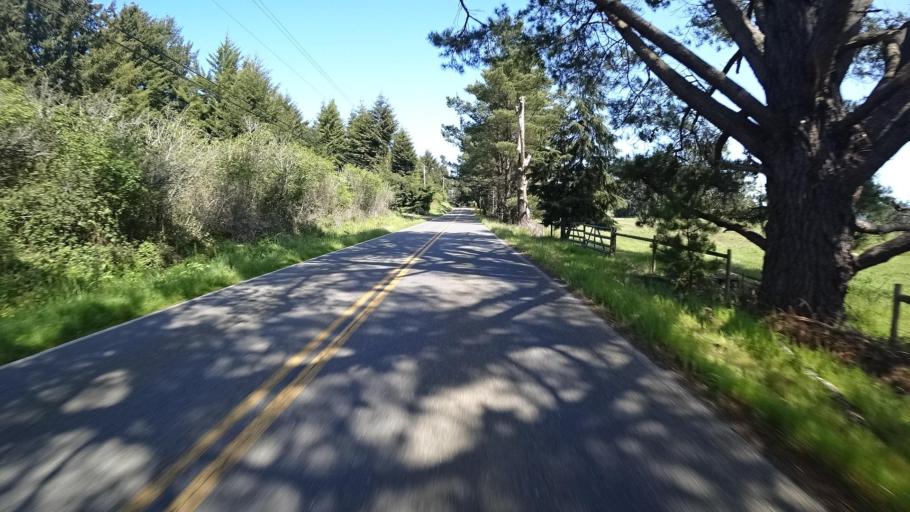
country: US
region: California
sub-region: Humboldt County
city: Hydesville
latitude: 40.5520
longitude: -124.1159
